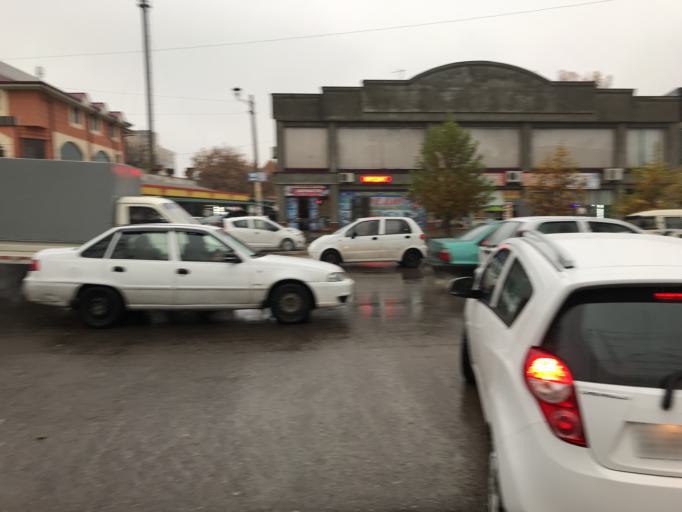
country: UZ
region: Toshkent
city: Yangiyul
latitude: 41.1170
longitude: 69.0565
